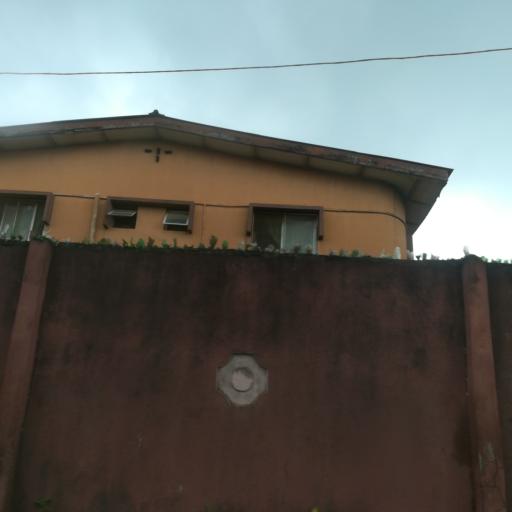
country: NG
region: Lagos
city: Agege
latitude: 6.5948
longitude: 3.3015
